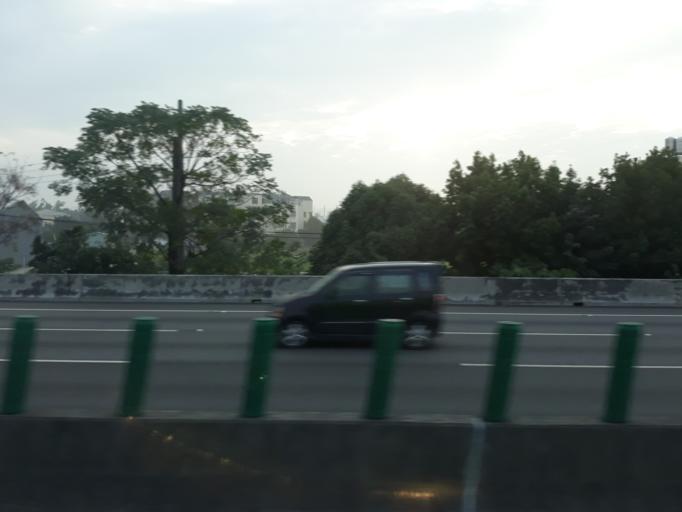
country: TW
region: Taiwan
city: Fengyuan
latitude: 24.2297
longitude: 120.6858
